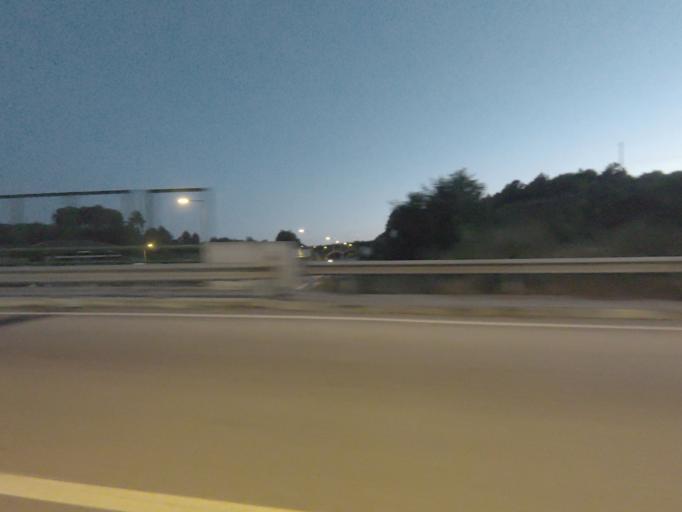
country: PT
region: Vila Real
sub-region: Vila Real
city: Vila Real
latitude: 41.2803
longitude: -7.7217
